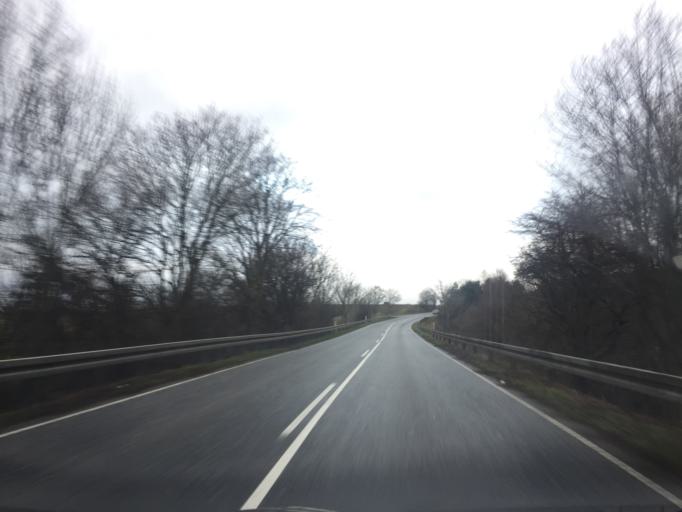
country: DK
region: Zealand
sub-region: Lejre Kommune
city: Ejby
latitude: 55.6515
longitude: 11.8104
